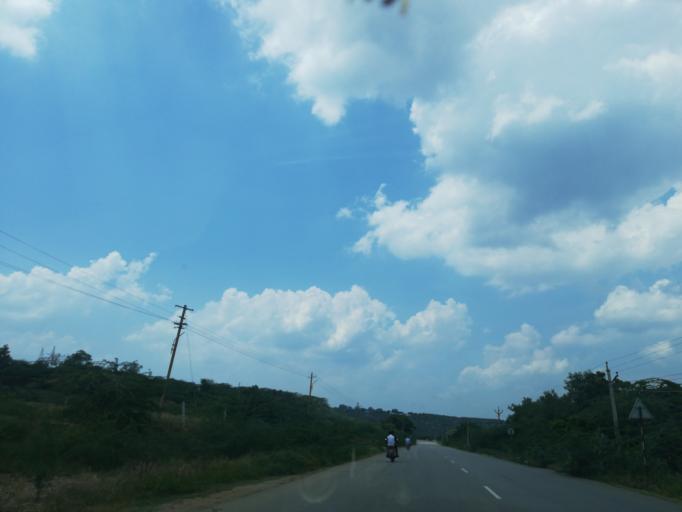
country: IN
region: Andhra Pradesh
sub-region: Guntur
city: Macherla
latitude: 16.5930
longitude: 79.3155
